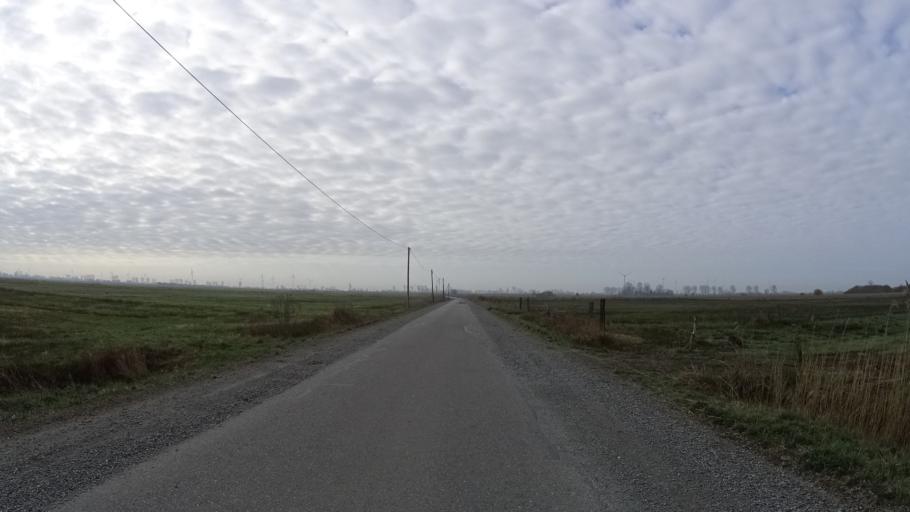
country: DE
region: Lower Saxony
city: Emden
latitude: 53.4079
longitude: 7.3057
